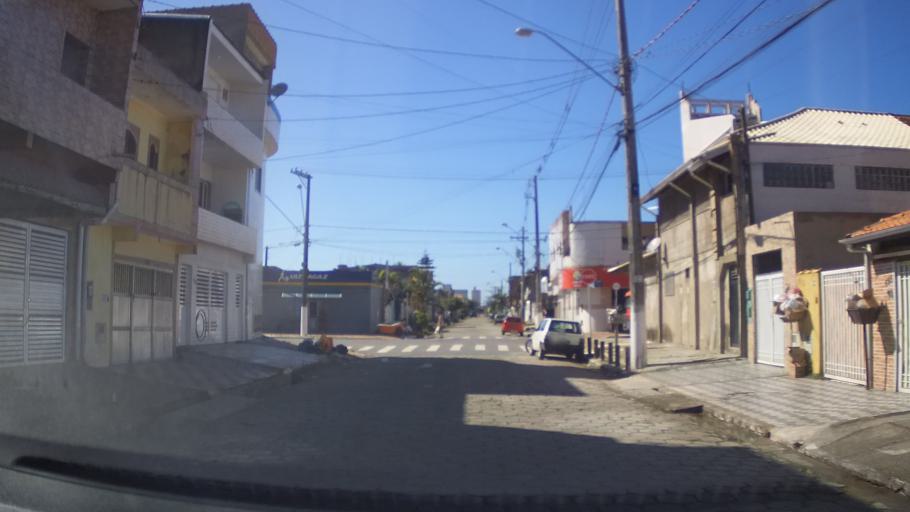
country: BR
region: Sao Paulo
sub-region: Praia Grande
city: Praia Grande
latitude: -24.0292
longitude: -46.5164
